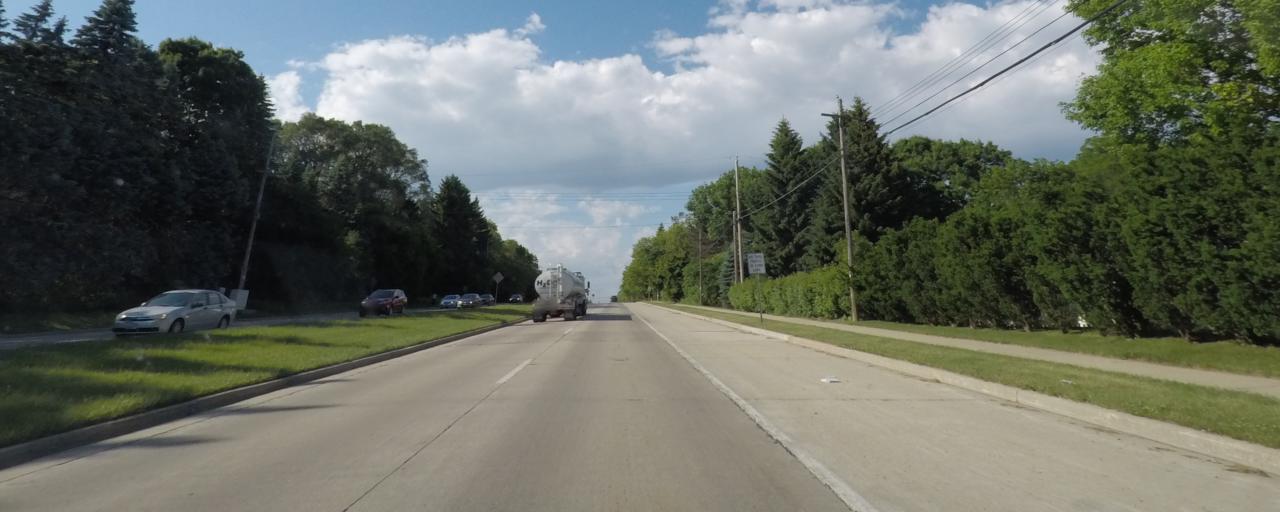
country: US
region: Wisconsin
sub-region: Milwaukee County
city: Greendale
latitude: 42.9351
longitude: -88.0083
